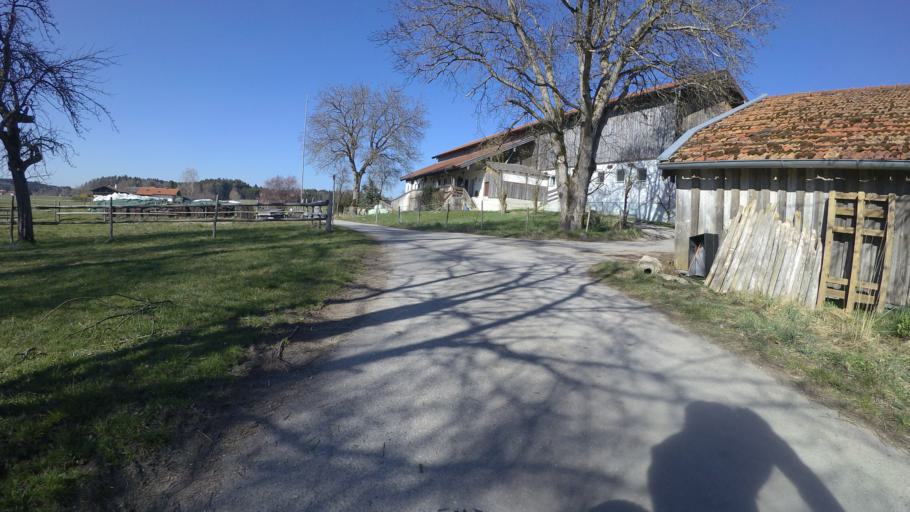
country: DE
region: Bavaria
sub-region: Upper Bavaria
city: Seeon-Seebruck
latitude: 47.9529
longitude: 12.5157
